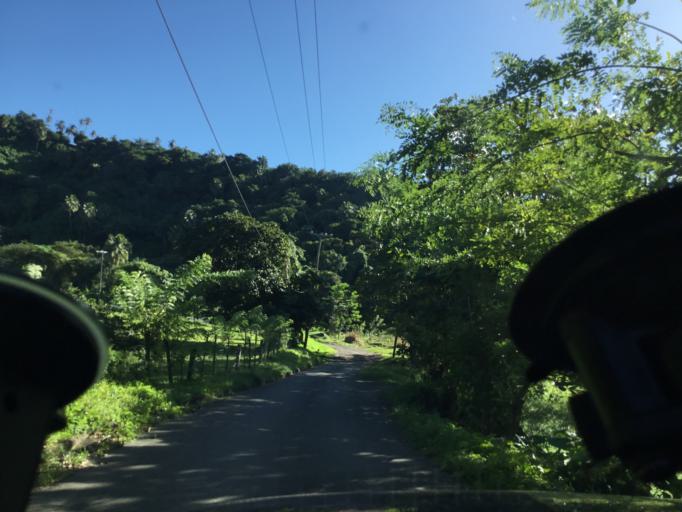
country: VC
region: Saint David
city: Chateaubelair
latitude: 13.3094
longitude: -61.2340
